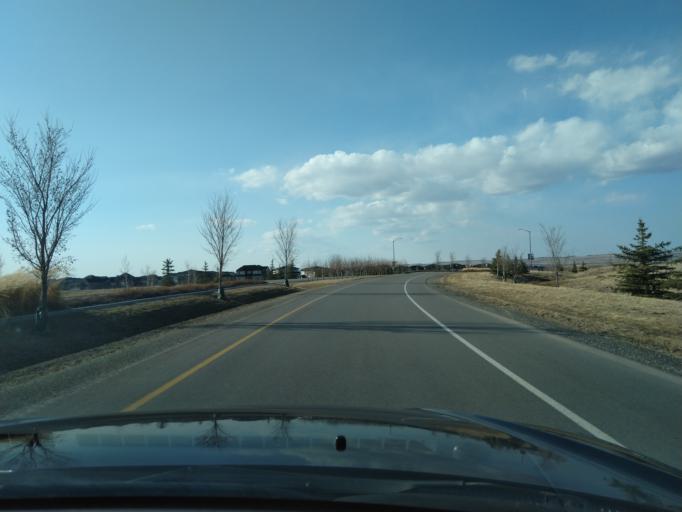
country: CA
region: Alberta
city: Cochrane
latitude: 51.1059
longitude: -114.3919
